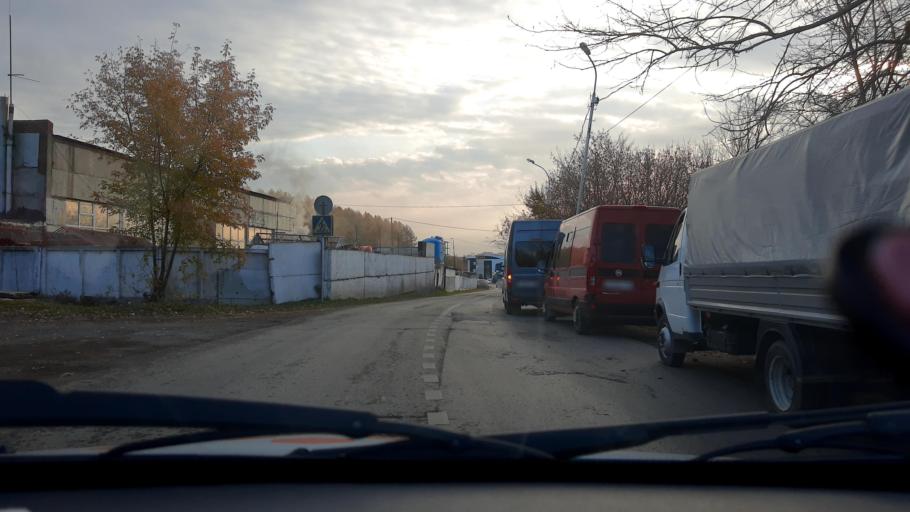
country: RU
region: Bashkortostan
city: Ufa
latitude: 54.8084
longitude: 56.0545
